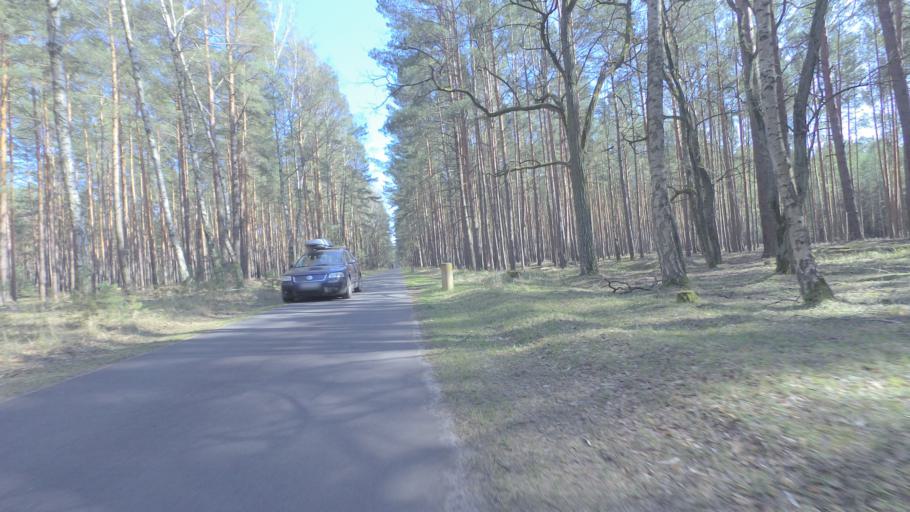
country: DE
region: Brandenburg
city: Halbe
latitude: 52.1711
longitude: 13.7527
